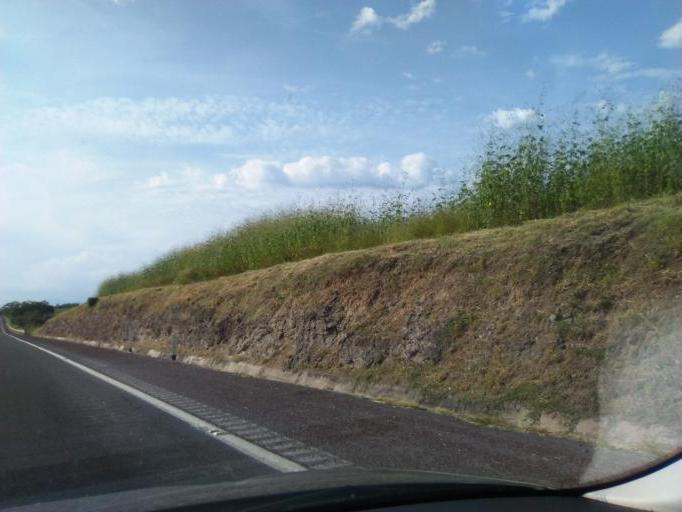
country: MX
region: Morelos
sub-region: Jojutla
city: Tehuixtla
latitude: 18.5977
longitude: -99.2757
